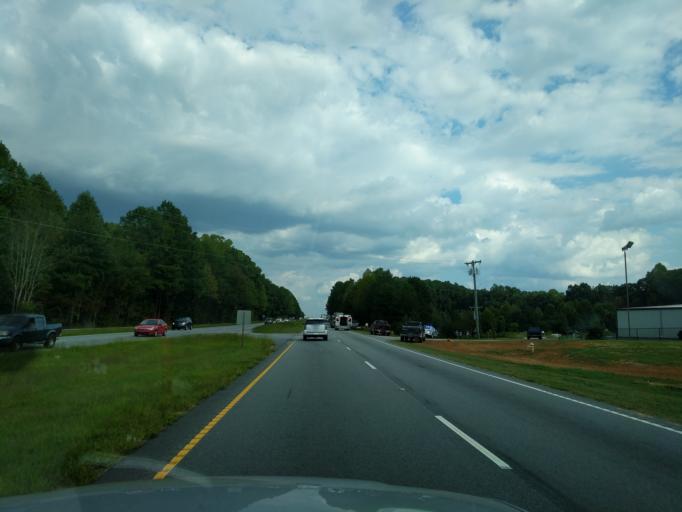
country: US
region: South Carolina
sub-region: Anderson County
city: Powdersville
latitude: 34.7937
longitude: -82.4998
